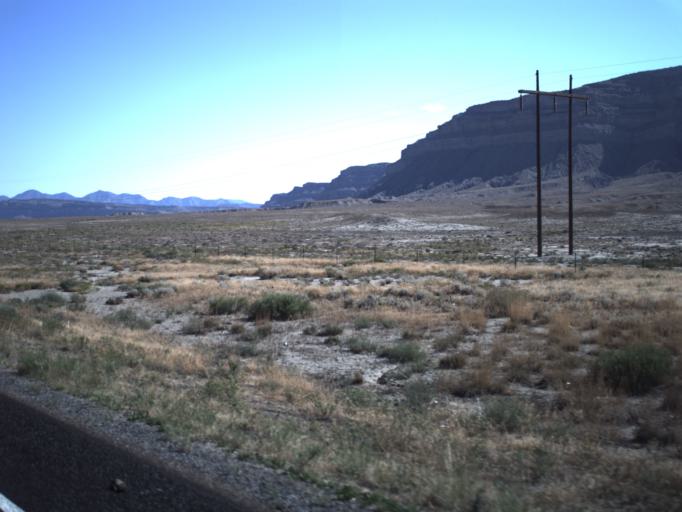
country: US
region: Utah
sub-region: Carbon County
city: East Carbon City
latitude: 39.1723
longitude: -110.3382
